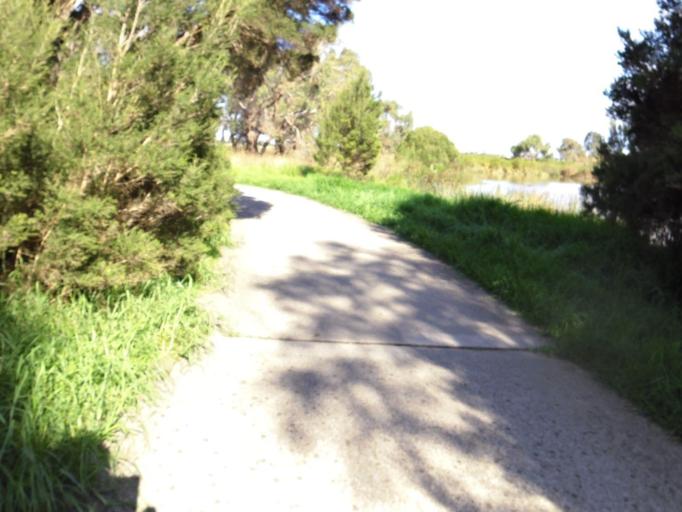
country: AU
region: Victoria
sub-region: Casey
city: Berwick
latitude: -38.0634
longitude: 145.3274
